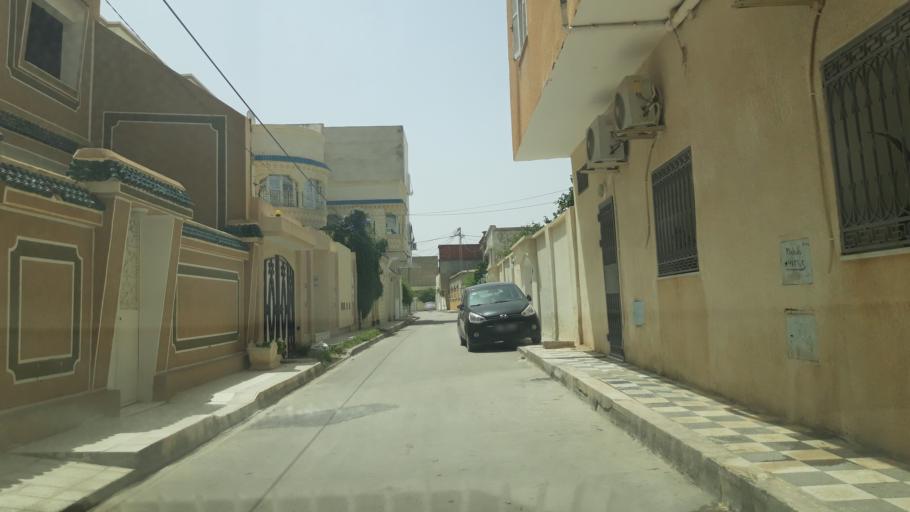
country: TN
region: Al Qayrawan
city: Kairouan
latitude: 35.6694
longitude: 10.0811
